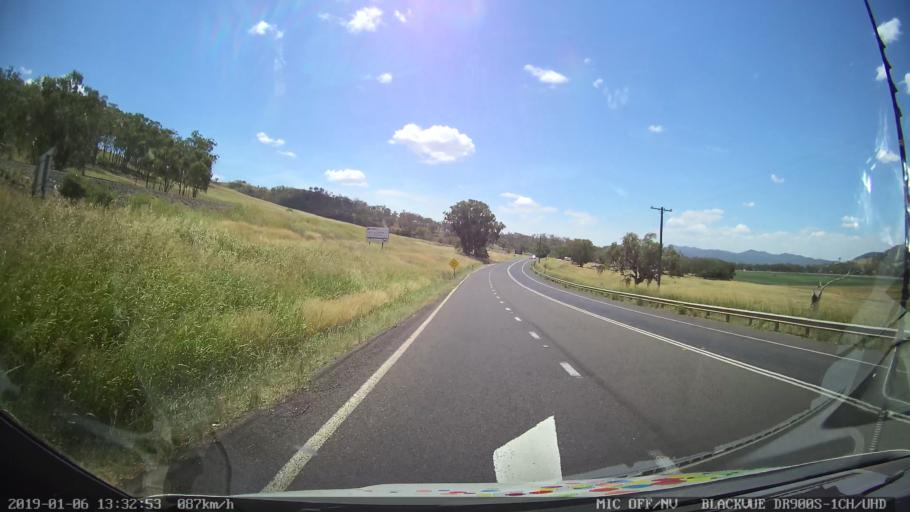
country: AU
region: New South Wales
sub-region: Tamworth Municipality
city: East Tamworth
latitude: -31.1055
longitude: 151.0016
